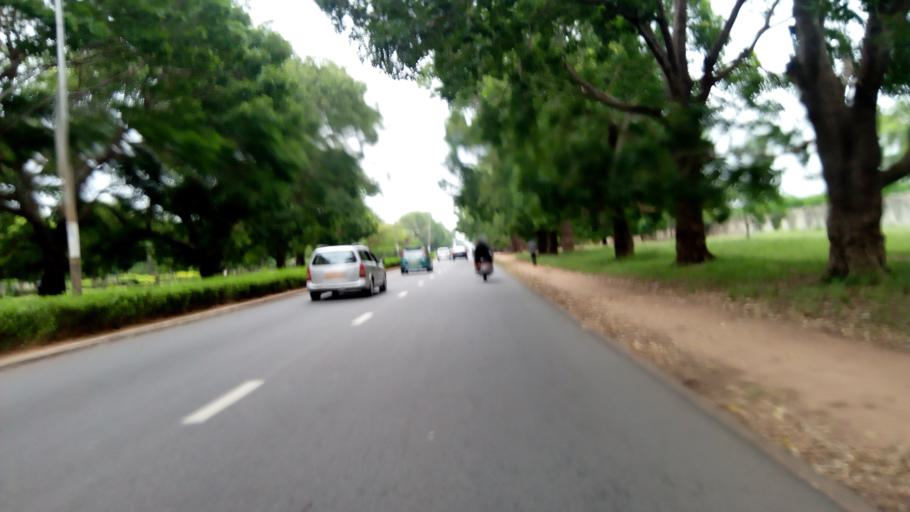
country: TG
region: Maritime
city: Lome
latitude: 6.1763
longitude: 1.2173
